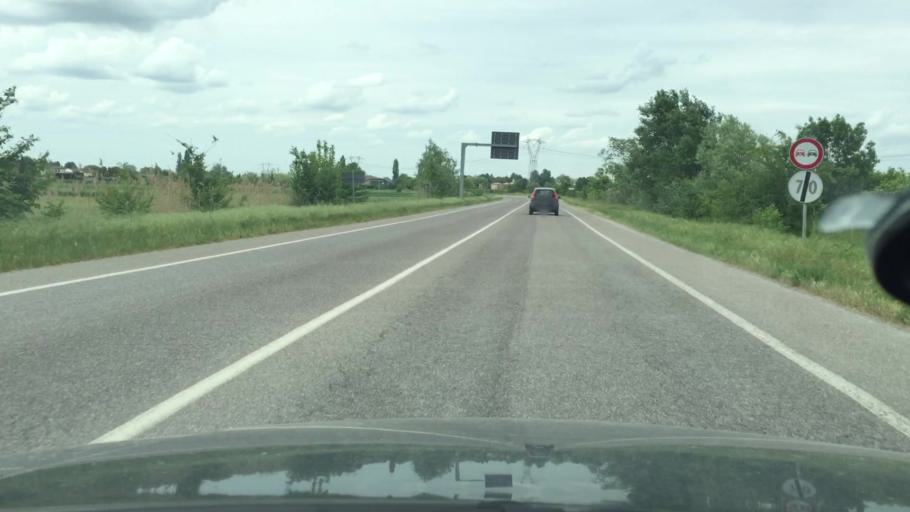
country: IT
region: Emilia-Romagna
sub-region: Provincia di Ferrara
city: Cona
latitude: 44.8068
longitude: 11.7192
